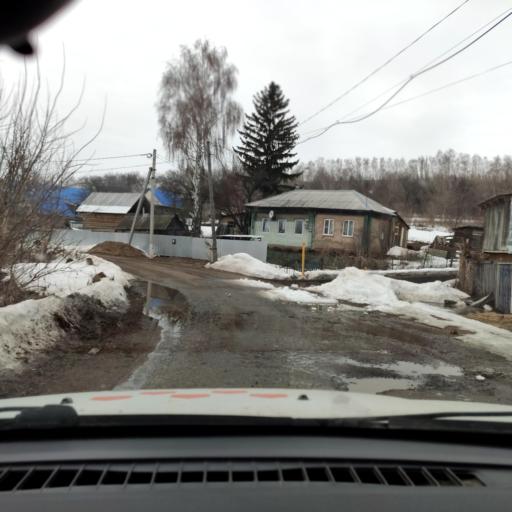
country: RU
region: Bashkortostan
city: Kushnarenkovo
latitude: 55.1188
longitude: 55.3510
